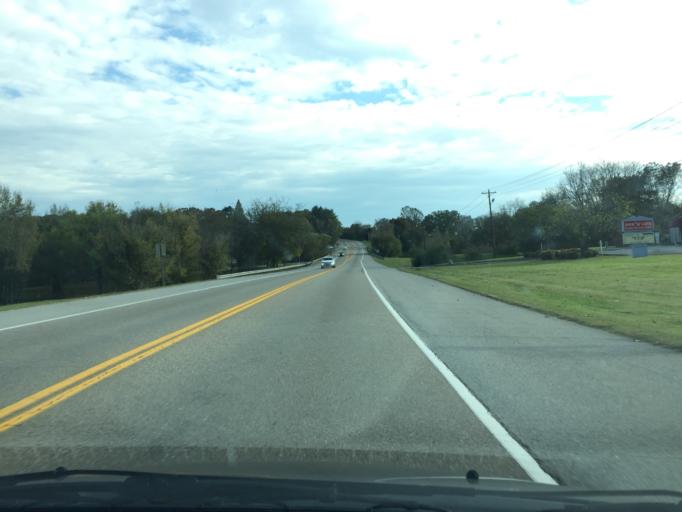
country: US
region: Tennessee
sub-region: Loudon County
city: Loudon
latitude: 35.7272
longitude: -84.3796
